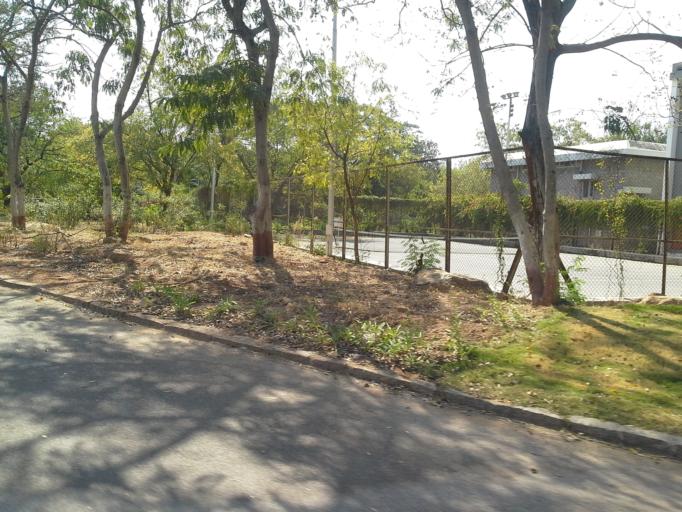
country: IN
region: Telangana
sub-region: Hyderabad
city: Hyderabad
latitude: 17.3102
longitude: 78.4113
